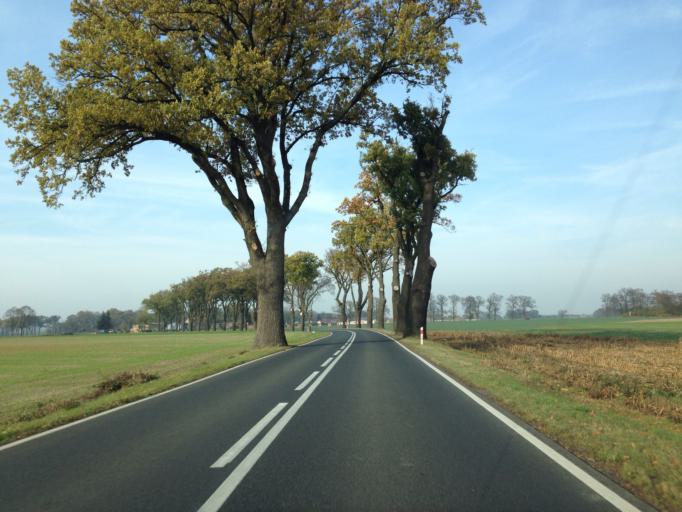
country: PL
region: Kujawsko-Pomorskie
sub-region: Powiat swiecki
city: Pruszcz
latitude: 53.2770
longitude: 18.1630
